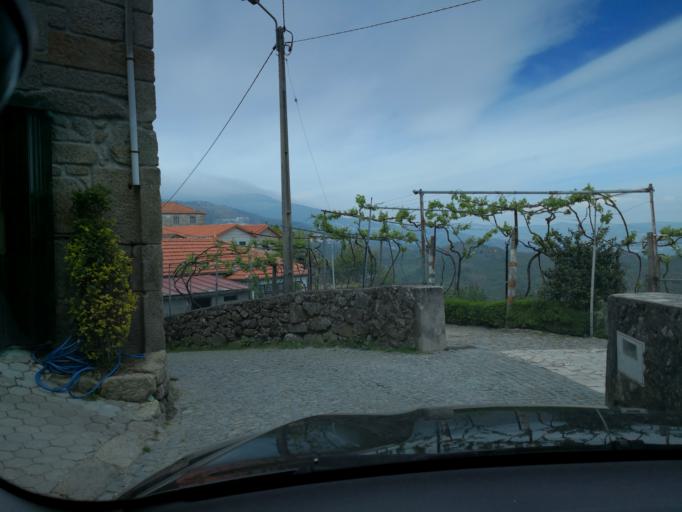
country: PT
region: Vila Real
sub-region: Vila Real
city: Vila Real
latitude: 41.3029
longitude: -7.8004
